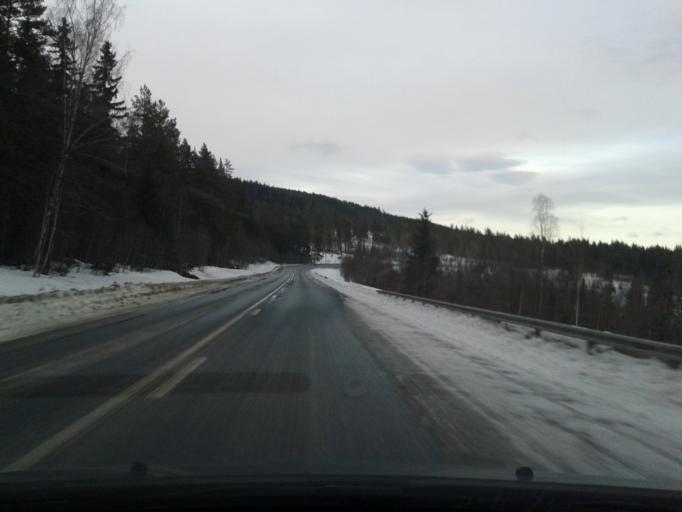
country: SE
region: Vaesternorrland
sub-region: Solleftea Kommun
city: Solleftea
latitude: 63.3330
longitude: 17.1272
